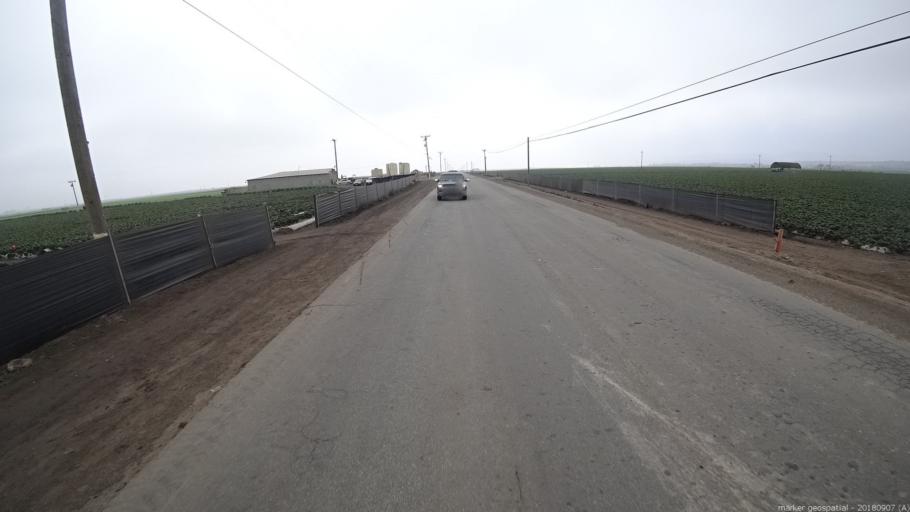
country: US
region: California
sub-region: Monterey County
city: Castroville
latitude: 36.7291
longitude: -121.7522
